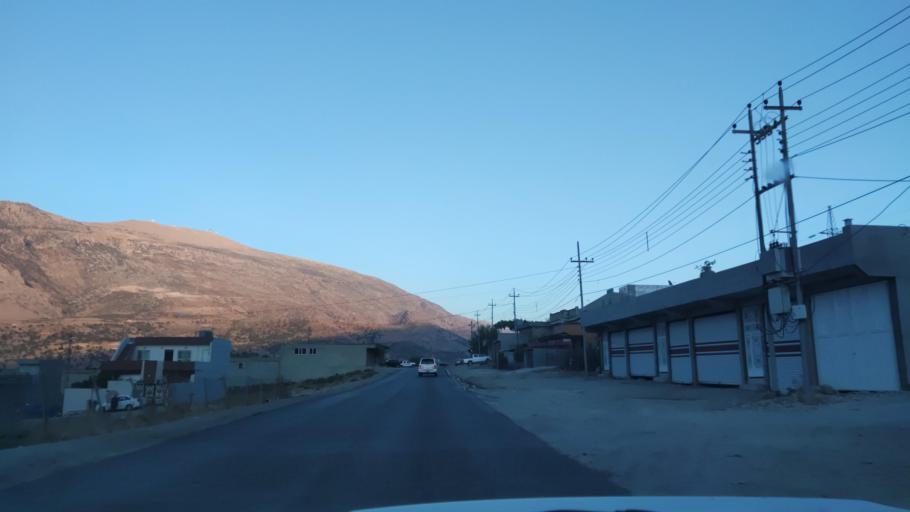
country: IQ
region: Arbil
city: Ruwandiz
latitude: 36.5905
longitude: 44.3884
